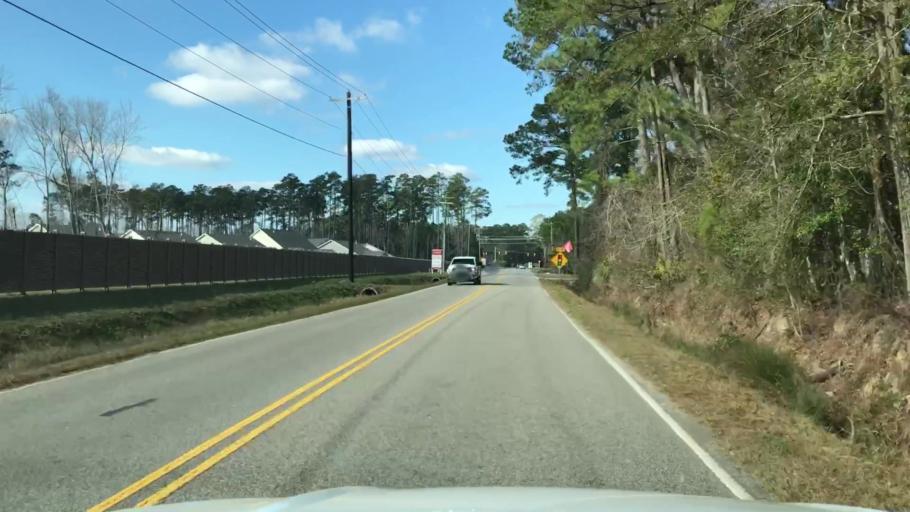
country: US
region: South Carolina
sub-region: Horry County
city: Socastee
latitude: 33.6595
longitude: -79.0086
